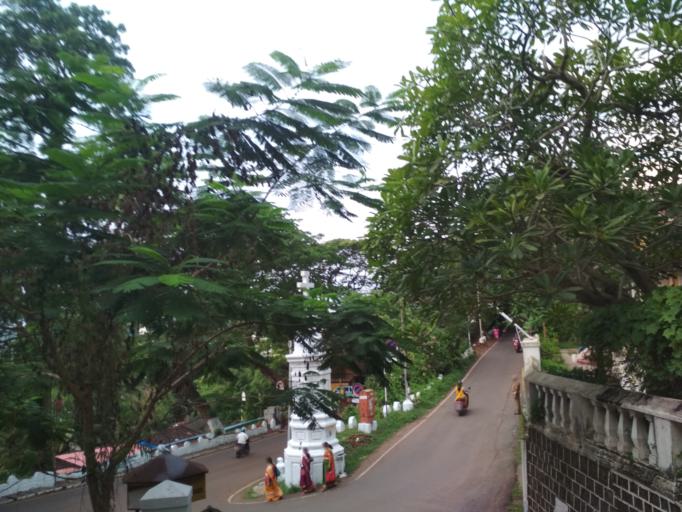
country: IN
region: Goa
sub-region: North Goa
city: Panaji
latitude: 15.4945
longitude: 73.8271
